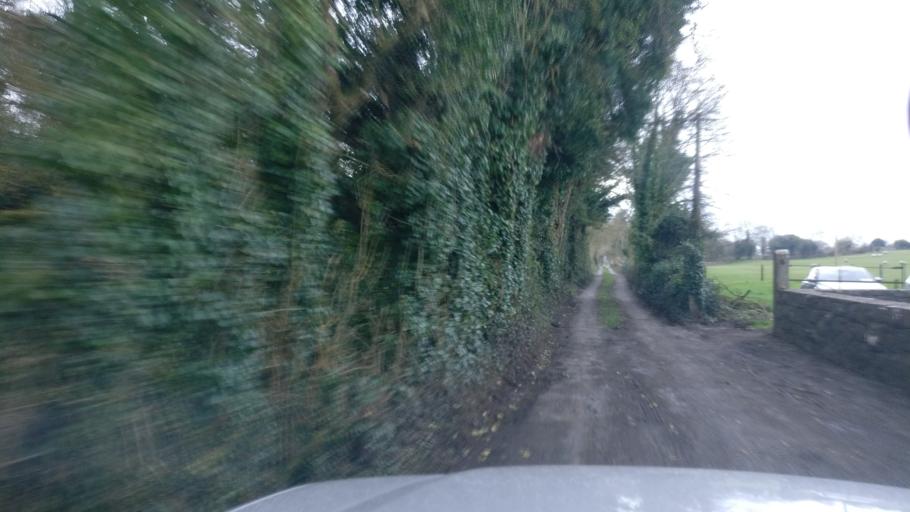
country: IE
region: Connaught
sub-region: County Galway
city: Loughrea
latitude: 53.2519
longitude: -8.4441
